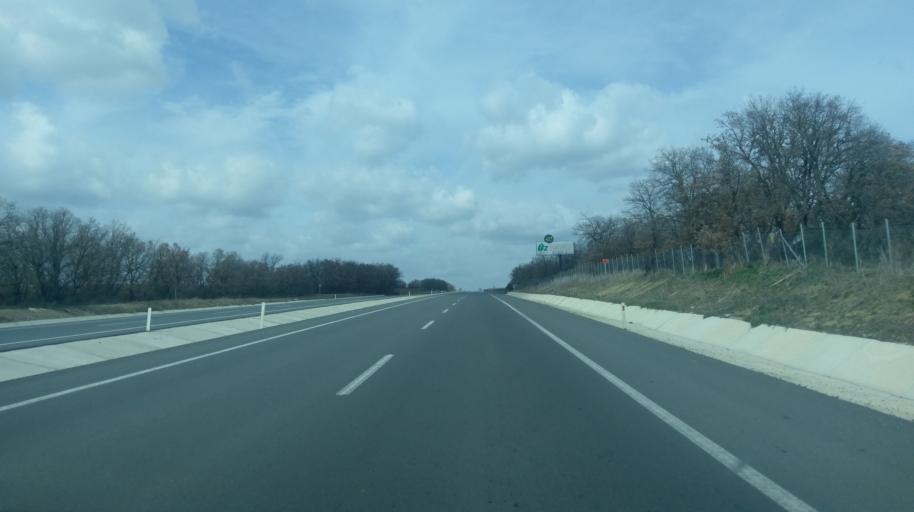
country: TR
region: Edirne
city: Kesan
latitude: 40.8956
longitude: 26.6338
